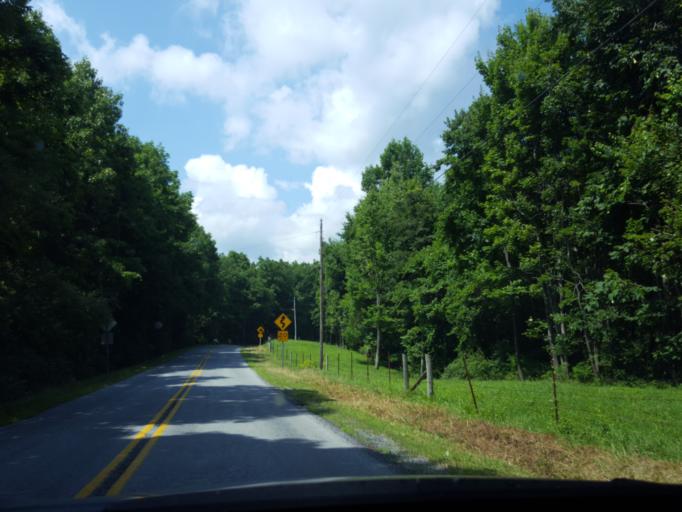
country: US
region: Virginia
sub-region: Nelson County
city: Nellysford
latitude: 37.9087
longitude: -78.9893
